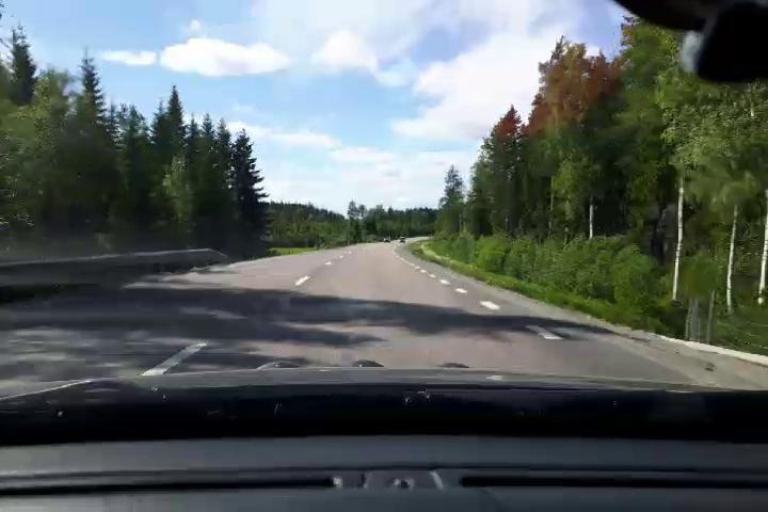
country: SE
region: Gaevleborg
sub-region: Bollnas Kommun
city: Bollnas
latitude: 61.3002
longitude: 16.4750
